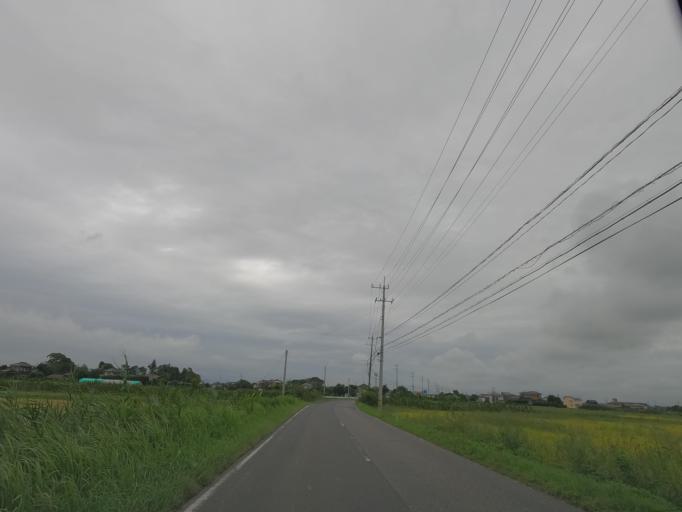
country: JP
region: Ibaraki
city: Toride
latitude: 35.9295
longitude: 140.0582
